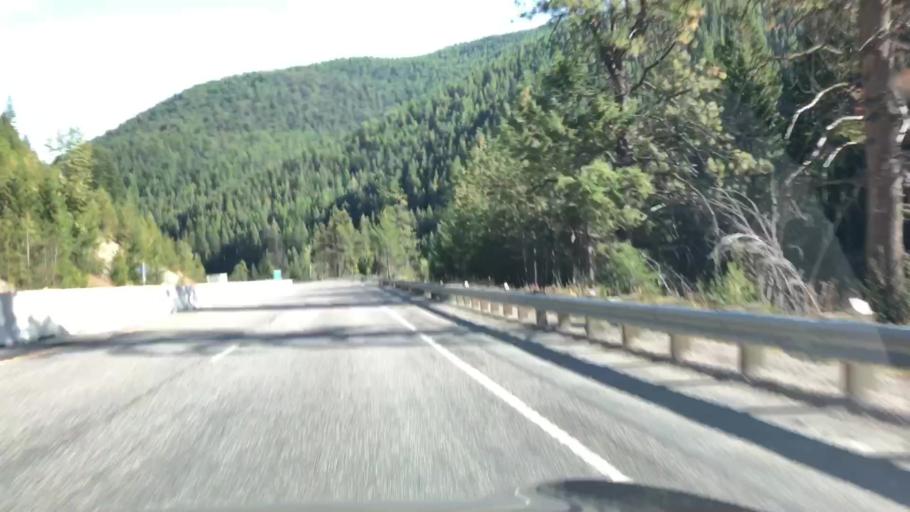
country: US
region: Montana
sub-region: Sanders County
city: Thompson Falls
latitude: 47.3967
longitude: -115.4559
